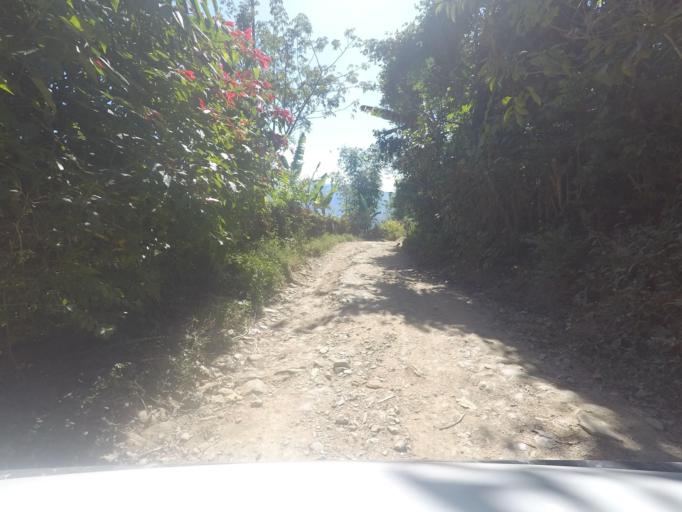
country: TL
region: Ermera
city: Gleno
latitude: -8.7311
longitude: 125.3402
